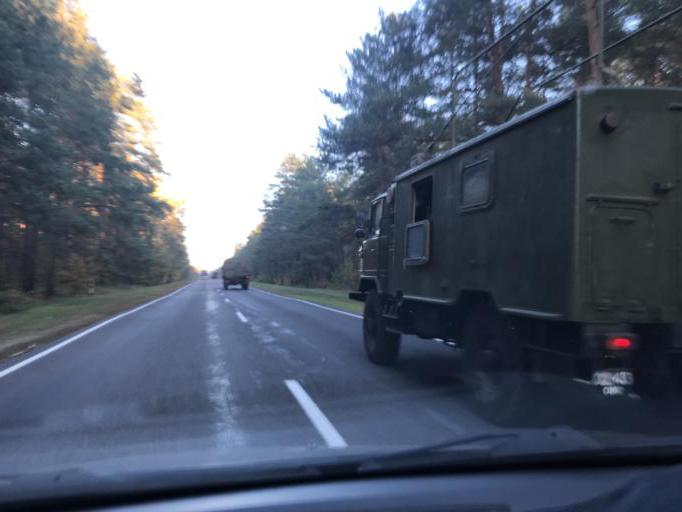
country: BY
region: Minsk
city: Staryya Darohi
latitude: 53.0440
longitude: 28.1333
